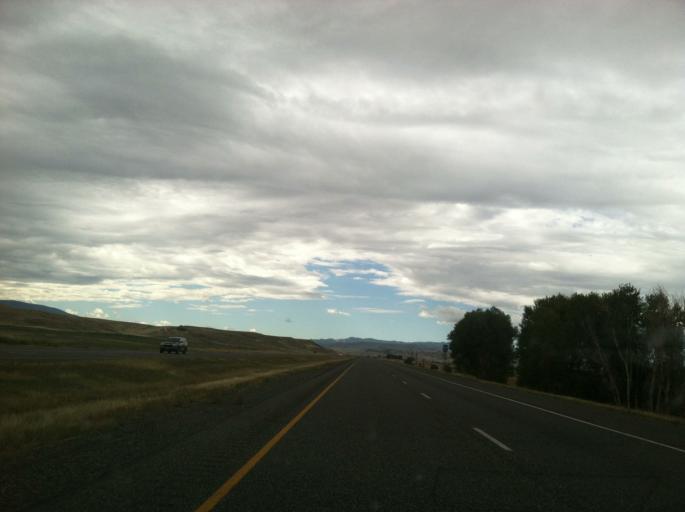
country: US
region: Montana
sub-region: Park County
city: Livingston
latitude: 45.7135
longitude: -110.4080
